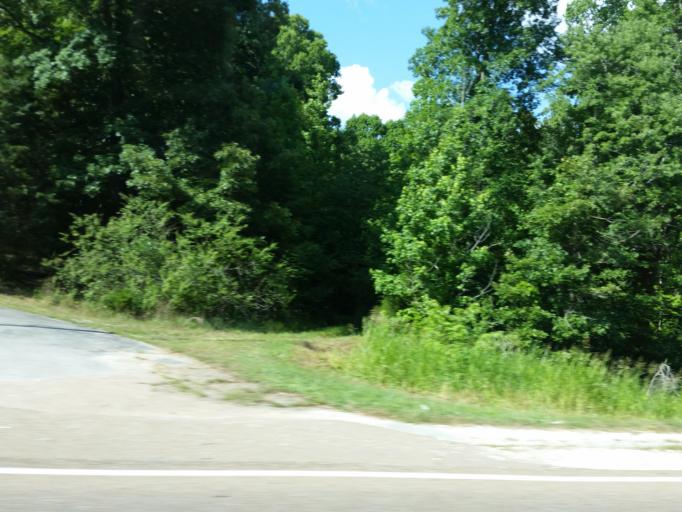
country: US
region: Tennessee
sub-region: Decatur County
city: Parsons
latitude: 35.6376
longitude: -88.0784
